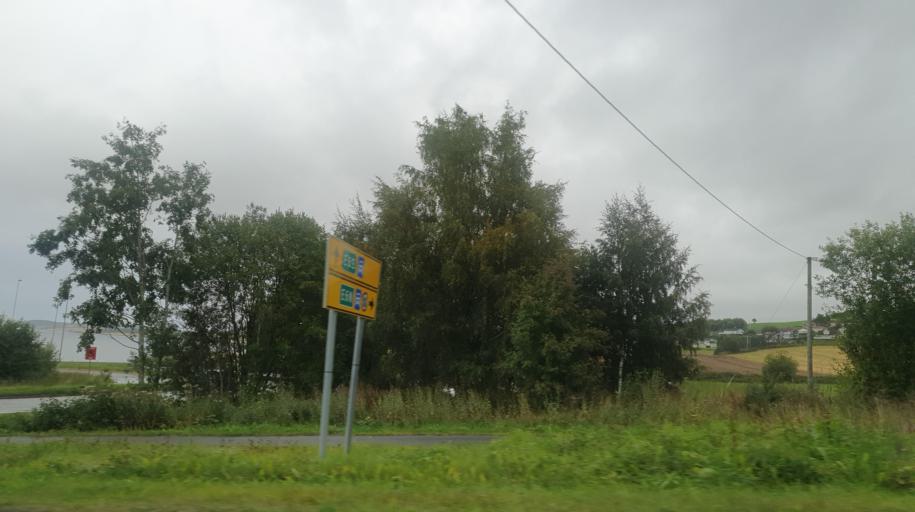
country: NO
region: Nord-Trondelag
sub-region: Levanger
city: Skogn
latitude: 63.7097
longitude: 11.1883
